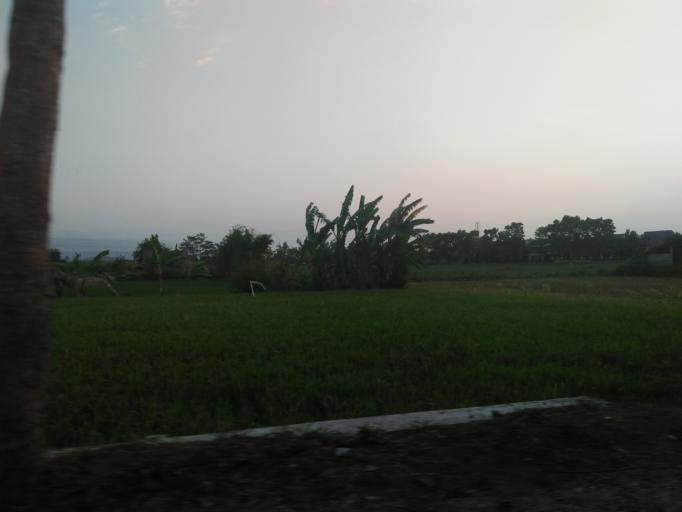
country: ID
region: Daerah Istimewa Yogyakarta
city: Sewon
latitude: -7.8476
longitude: 110.4092
